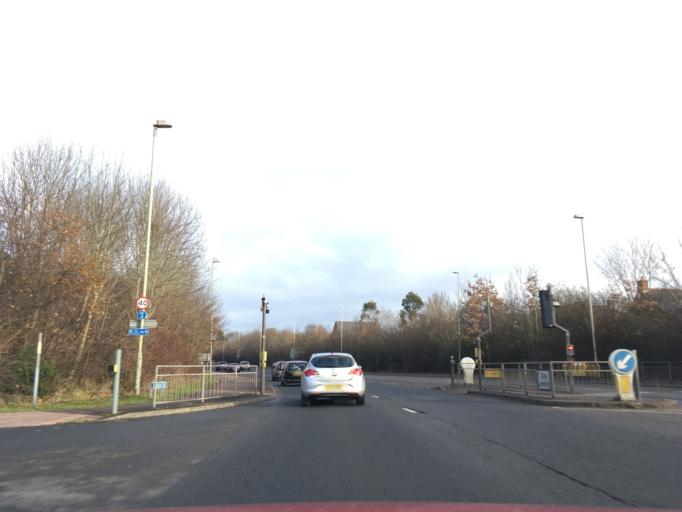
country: GB
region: England
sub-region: Gloucestershire
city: Gloucester
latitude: 51.8465
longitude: -2.2654
